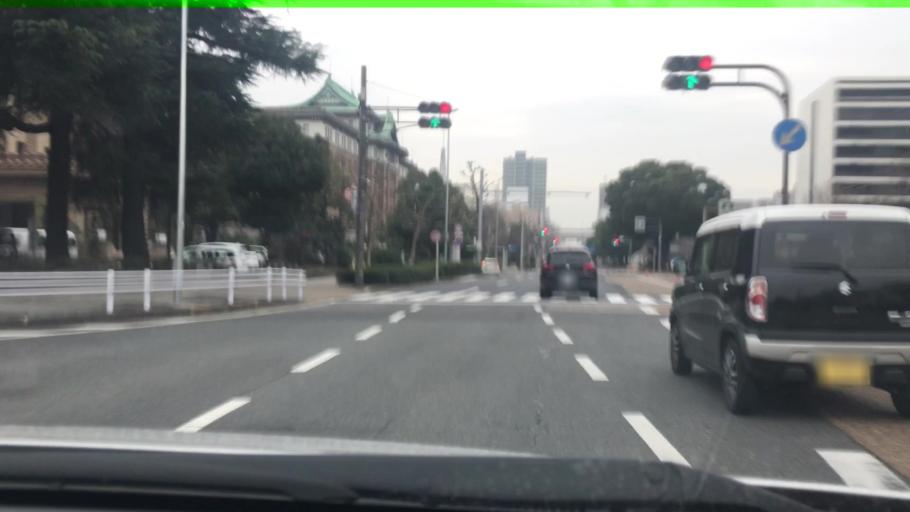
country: JP
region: Aichi
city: Nagoya-shi
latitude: 35.1819
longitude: 136.9055
